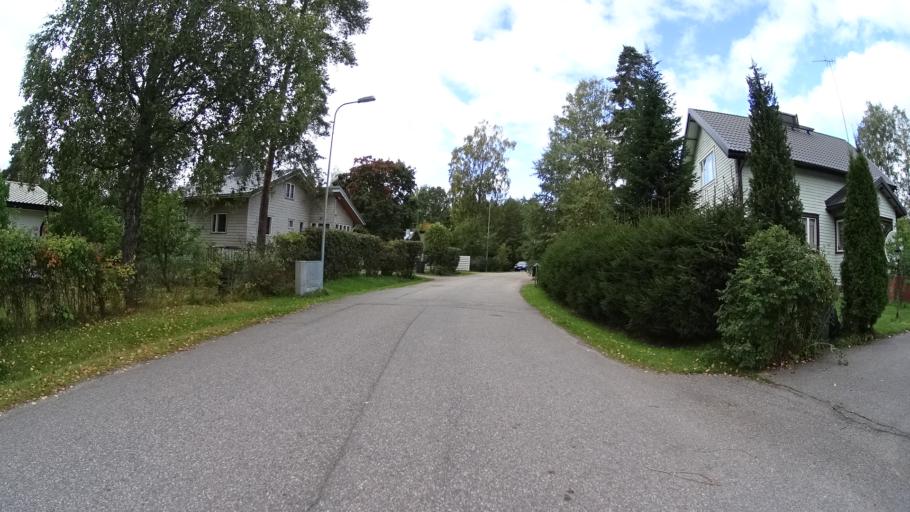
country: FI
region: Uusimaa
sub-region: Helsinki
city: Helsinki
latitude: 60.2499
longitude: 24.9016
